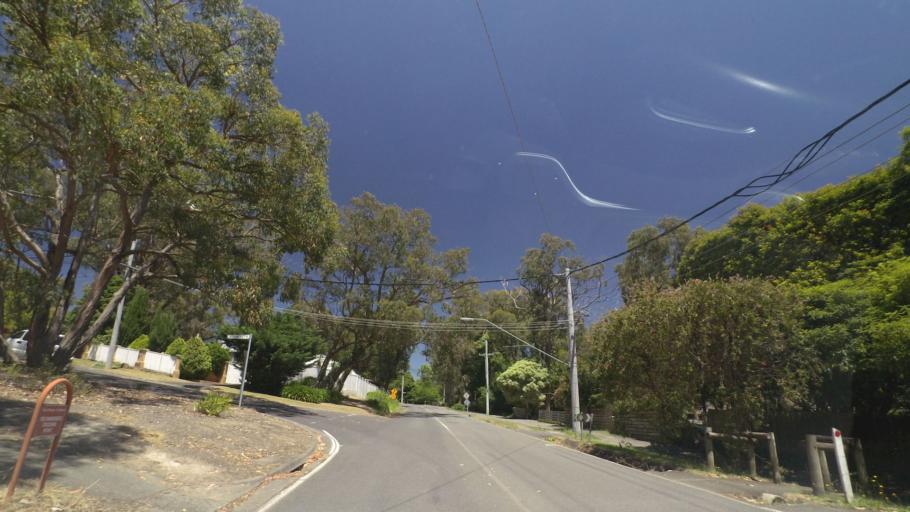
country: AU
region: Victoria
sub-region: Yarra Ranges
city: Montrose
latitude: -37.8166
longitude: 145.3420
